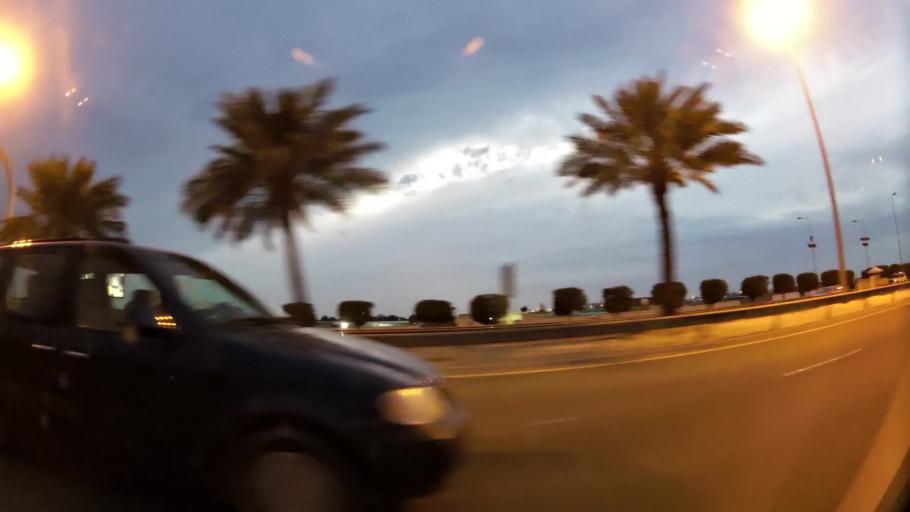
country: BH
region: Northern
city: Madinat `Isa
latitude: 26.1712
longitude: 50.5027
